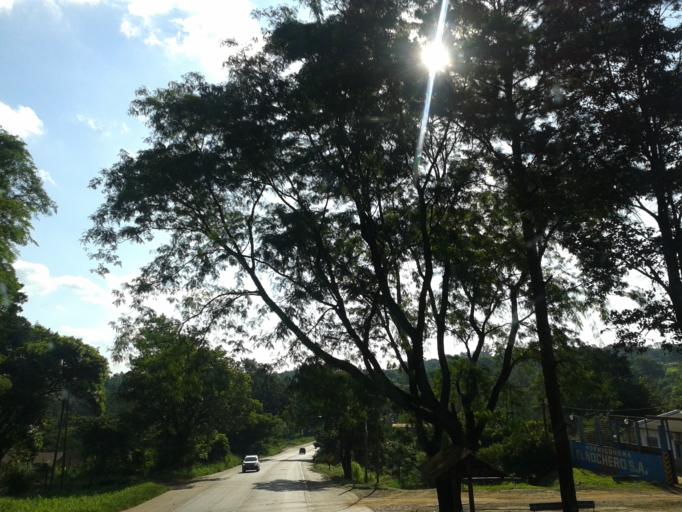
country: AR
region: Misiones
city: Guarani
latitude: -27.4932
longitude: -55.1608
